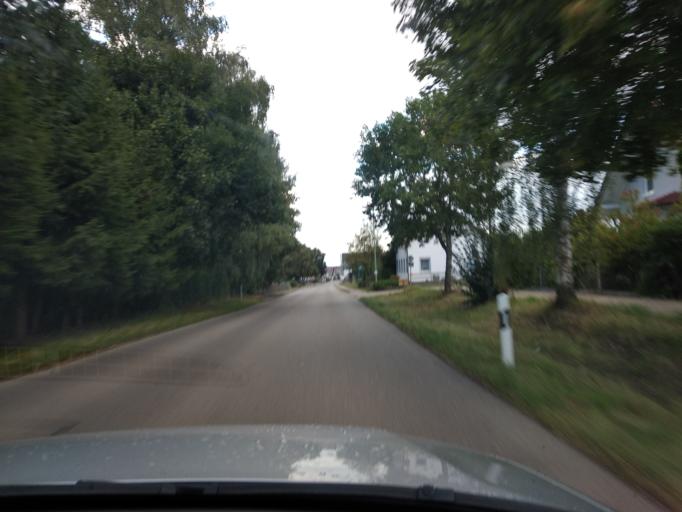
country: DE
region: Bavaria
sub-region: Swabia
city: Woringen
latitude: 47.9187
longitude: 10.2026
